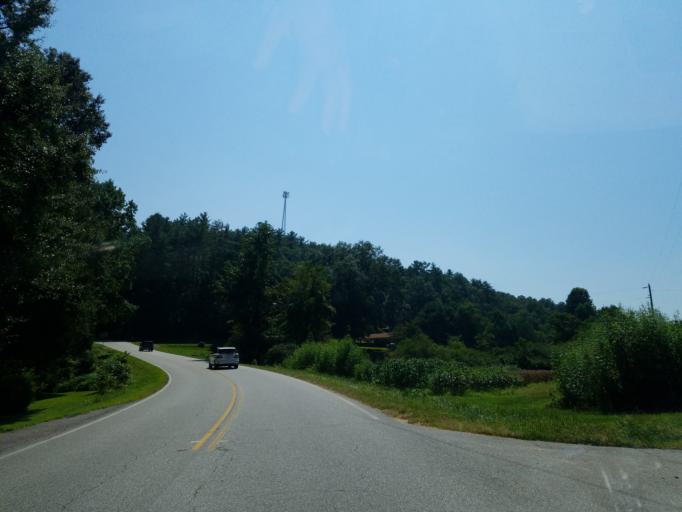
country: US
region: Georgia
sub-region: Lumpkin County
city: Dahlonega
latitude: 34.6584
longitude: -83.9080
